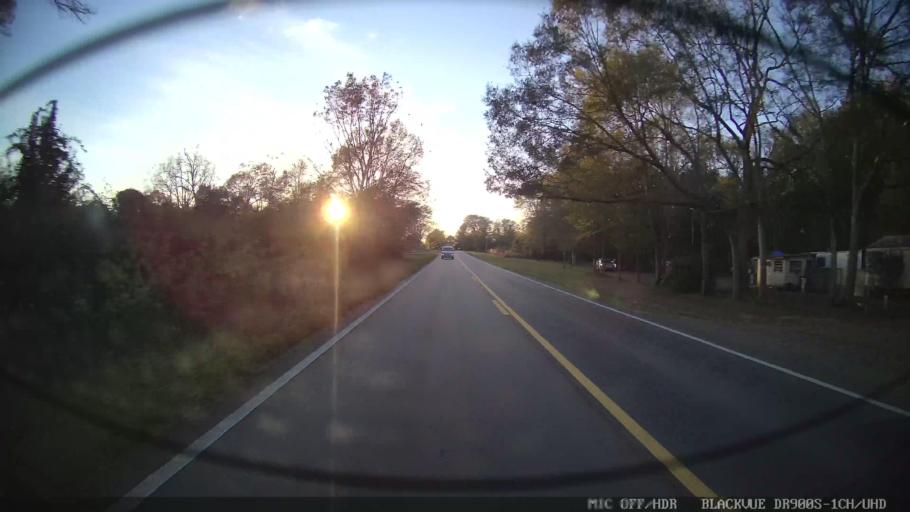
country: US
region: Mississippi
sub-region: Lamar County
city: Lumberton
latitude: 31.0007
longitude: -89.3397
